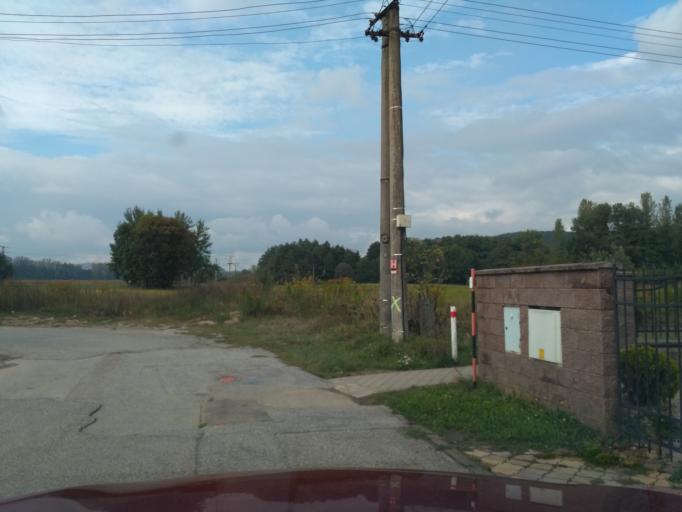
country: SK
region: Kosicky
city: Kosice
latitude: 48.6414
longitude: 21.1684
